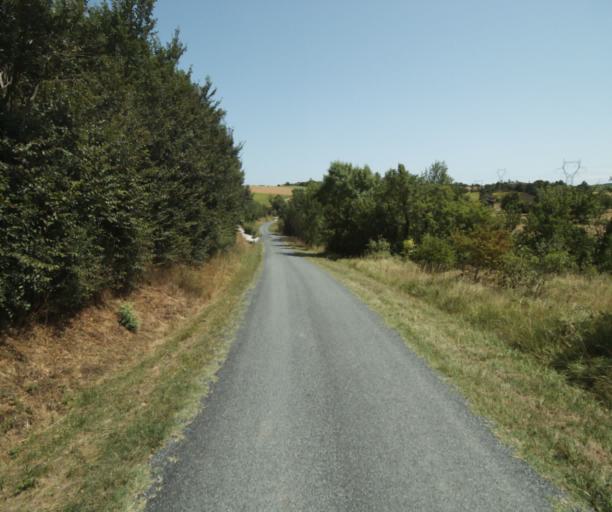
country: FR
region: Midi-Pyrenees
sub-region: Departement de la Haute-Garonne
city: Auriac-sur-Vendinelle
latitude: 43.4607
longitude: 1.8237
